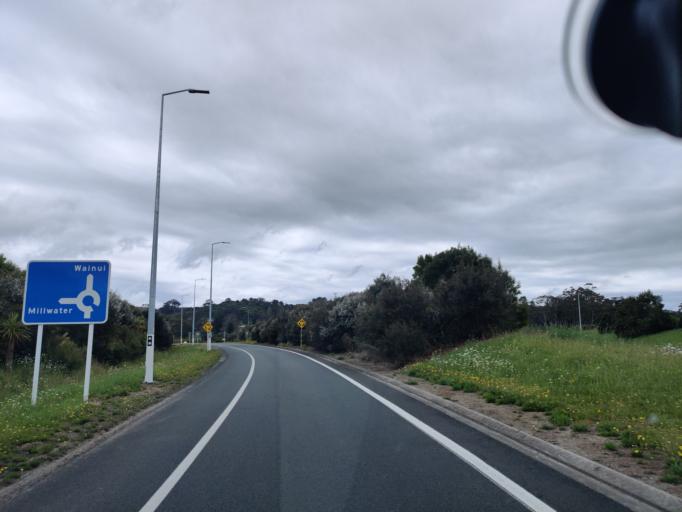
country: NZ
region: Auckland
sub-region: Auckland
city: Rothesay Bay
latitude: -36.6023
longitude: 174.6619
